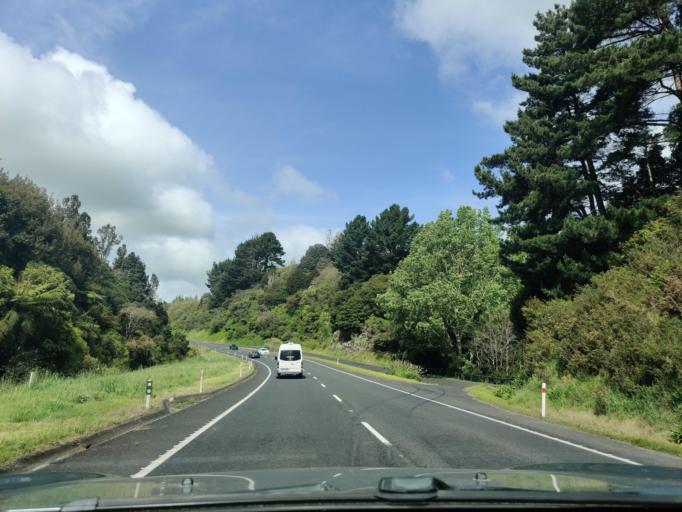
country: NZ
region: Manawatu-Wanganui
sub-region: Wanganui District
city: Wanganui
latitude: -39.8234
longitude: 174.8402
